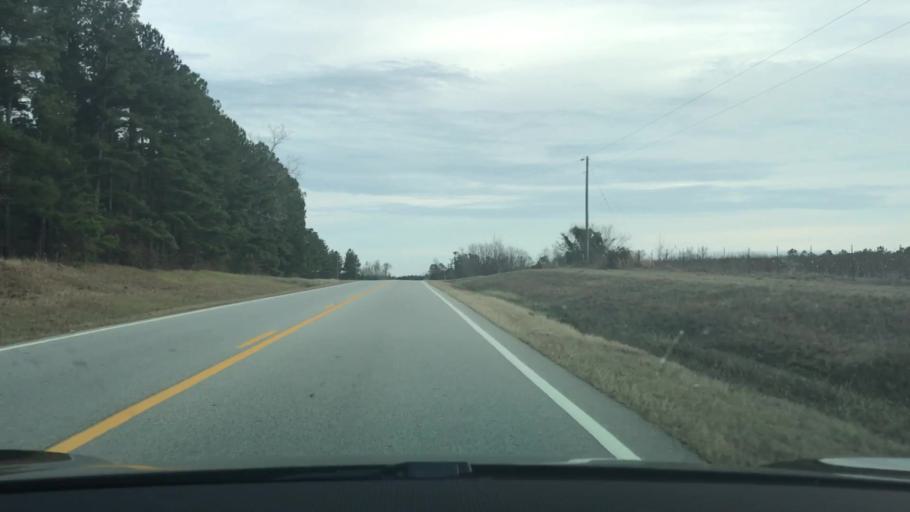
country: US
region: Georgia
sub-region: Glascock County
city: Gibson
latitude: 33.2727
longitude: -82.4985
